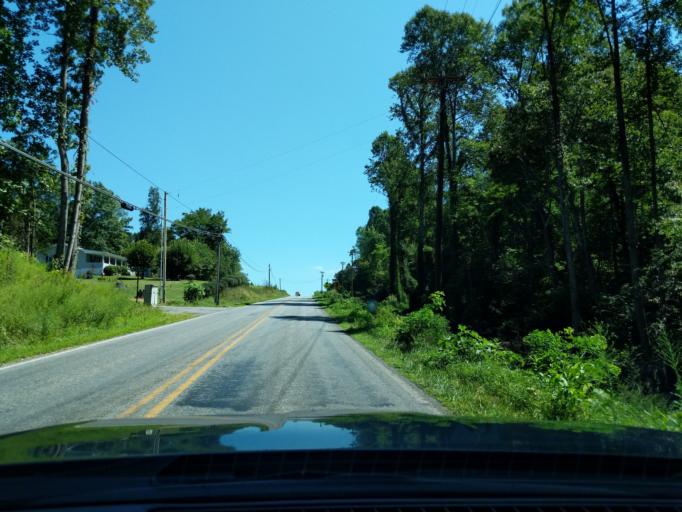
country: US
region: Georgia
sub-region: Towns County
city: Hiawassee
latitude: 35.0135
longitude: -83.7390
